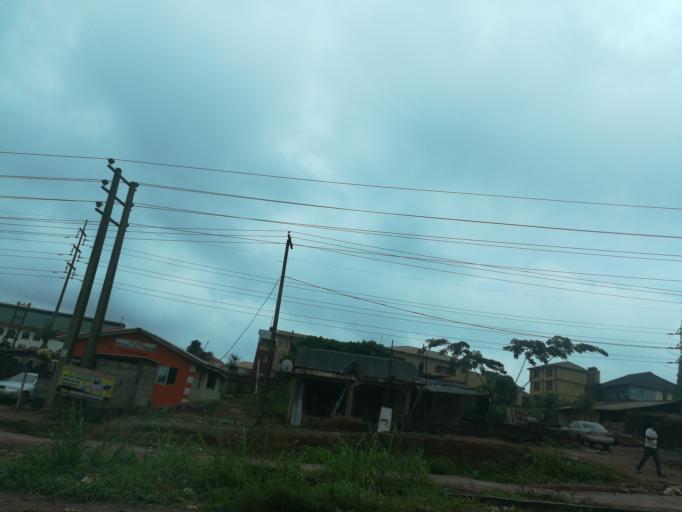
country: NG
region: Lagos
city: Ikorodu
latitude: 6.6422
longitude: 3.5158
